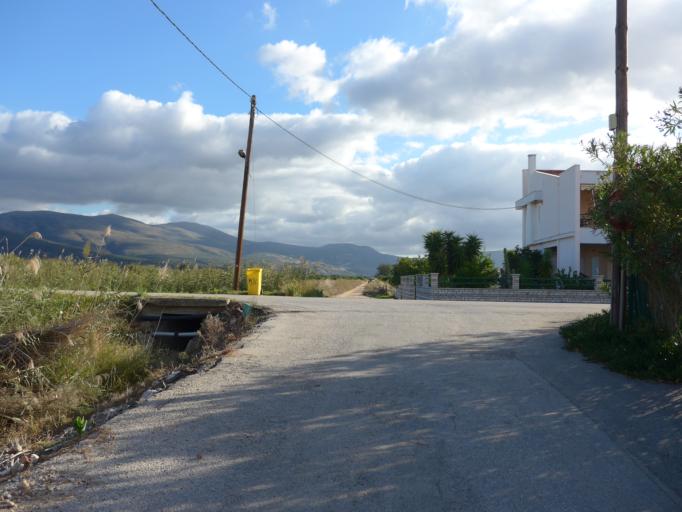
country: GR
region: Peloponnese
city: Asklipieio
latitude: 37.4894
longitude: 22.9922
